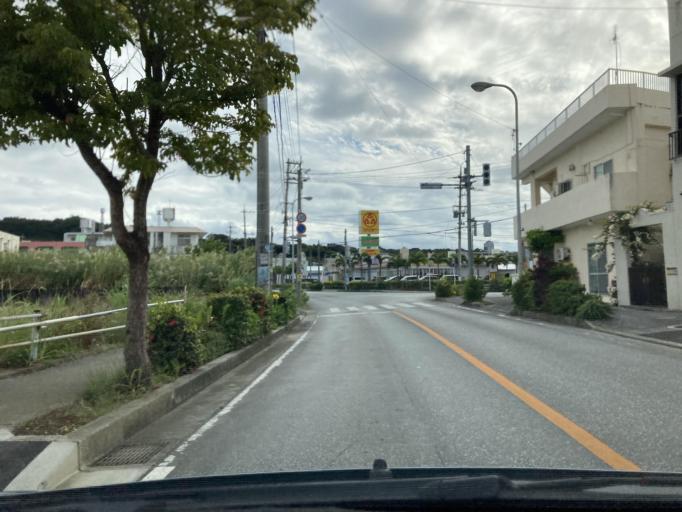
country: JP
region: Okinawa
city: Itoman
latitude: 26.1269
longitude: 127.6773
